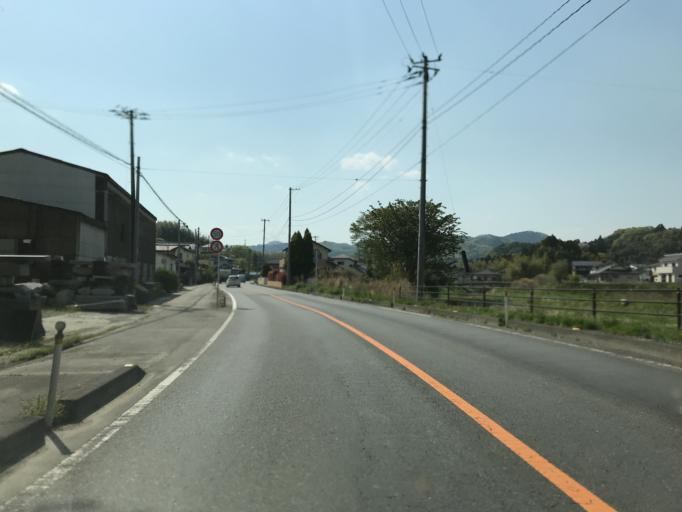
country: JP
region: Fukushima
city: Iwaki
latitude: 36.9517
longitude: 140.7674
